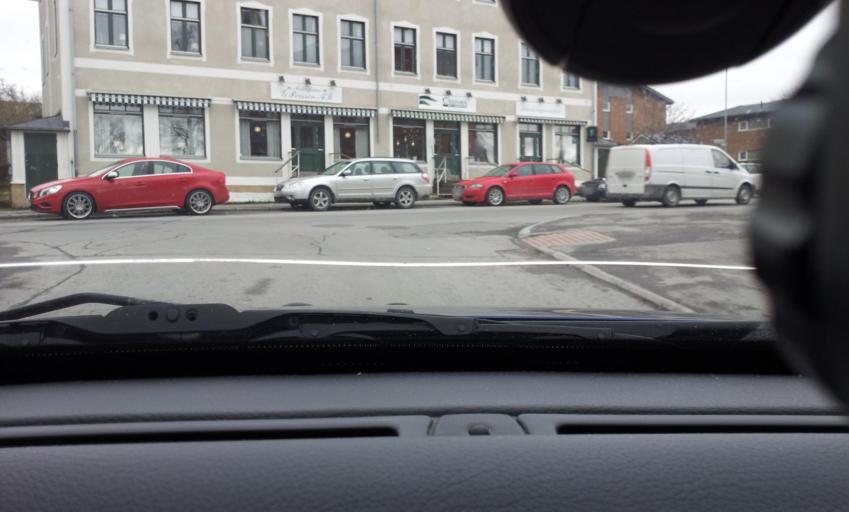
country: SE
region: Jaemtland
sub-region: OEstersunds Kommun
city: Ostersund
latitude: 63.1722
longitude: 14.6424
